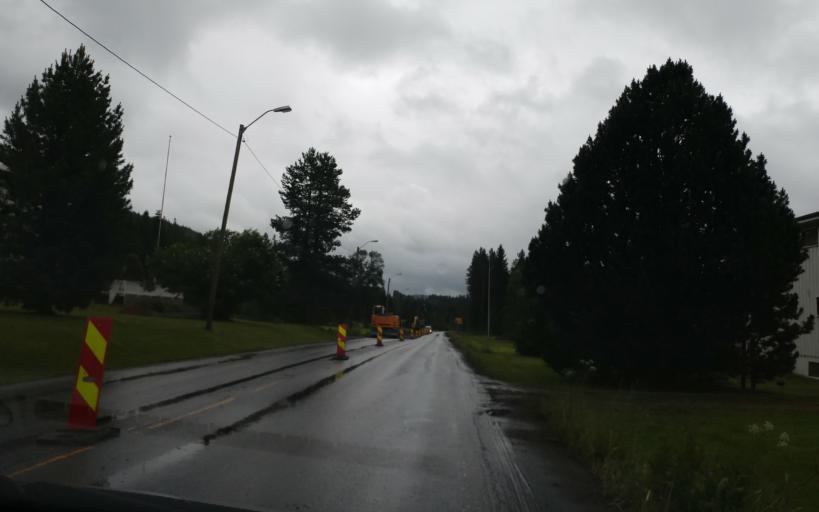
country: NO
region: Sor-Trondelag
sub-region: Selbu
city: Mebonden
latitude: 63.2827
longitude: 11.0804
